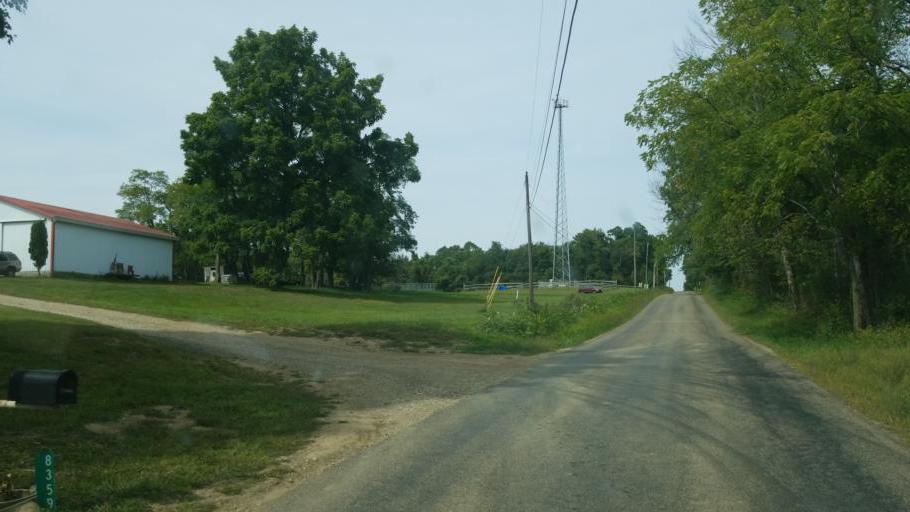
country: US
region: Ohio
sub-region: Knox County
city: Centerburg
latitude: 40.3631
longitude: -82.6060
